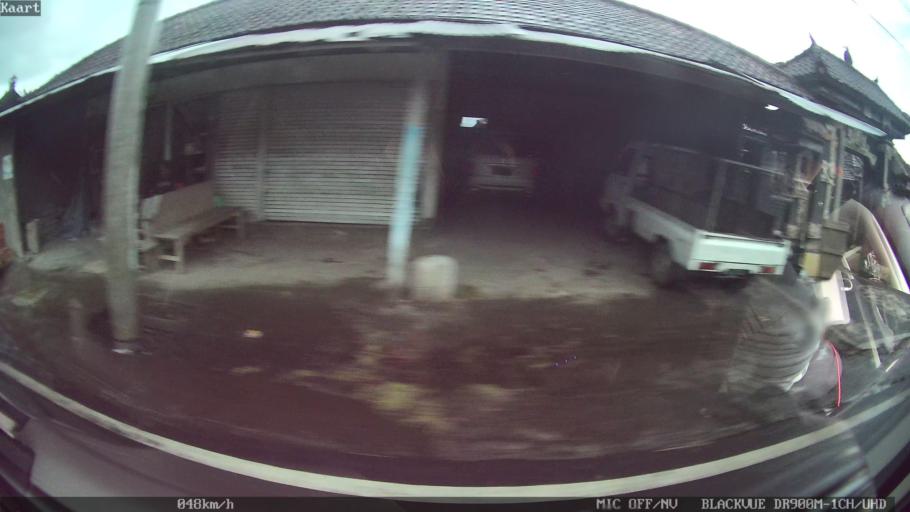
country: ID
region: Bali
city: Banjar Teguan
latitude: -8.5067
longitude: 115.2303
